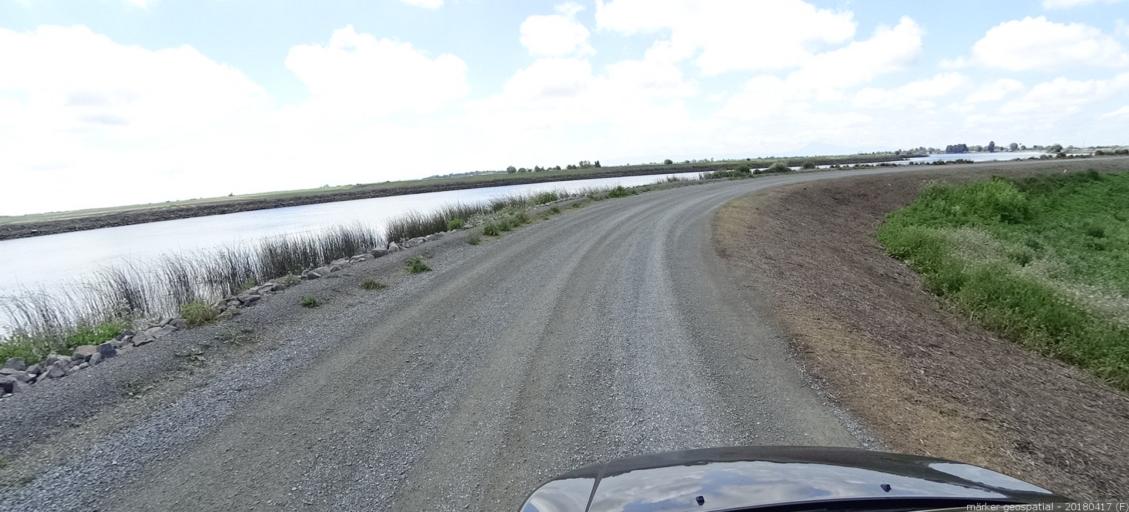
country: US
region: California
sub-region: Sacramento County
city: Walnut Grove
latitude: 38.1377
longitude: -121.5583
